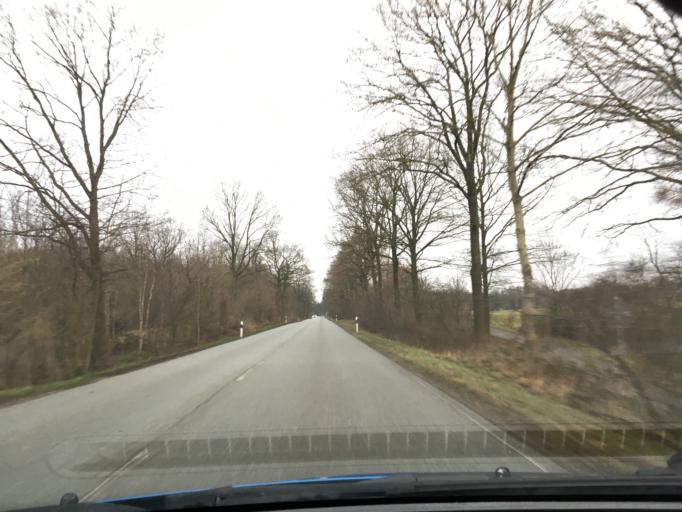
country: DE
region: Schleswig-Holstein
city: Siebeneichen
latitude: 53.5237
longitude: 10.6212
